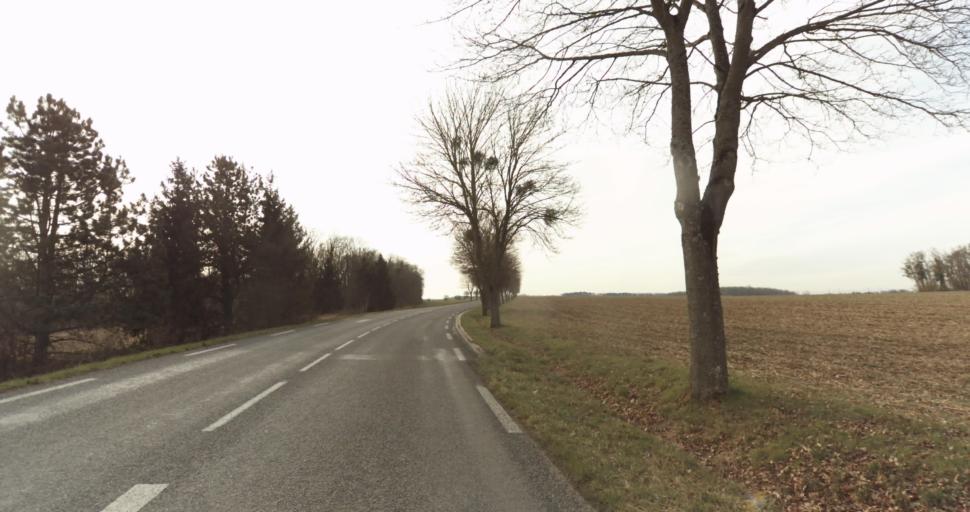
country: FR
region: Lorraine
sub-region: Departement de Meurthe-et-Moselle
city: Jarny
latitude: 49.1334
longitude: 5.8929
